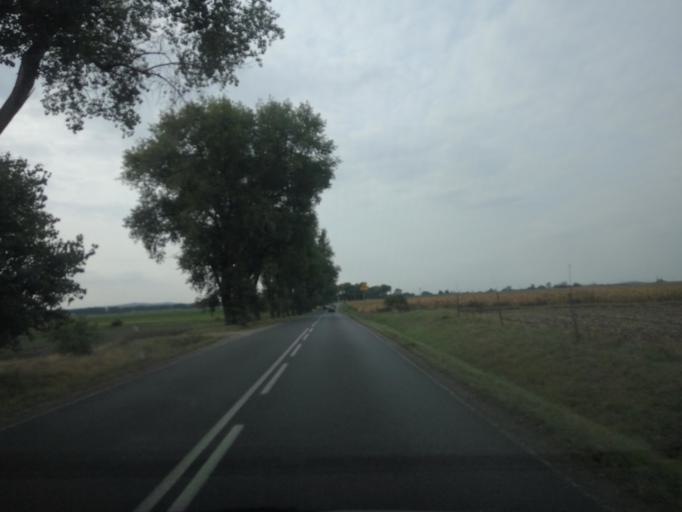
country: PL
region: Lower Silesian Voivodeship
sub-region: Powiat strzelinski
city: Strzelin
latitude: 50.8245
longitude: 17.0608
